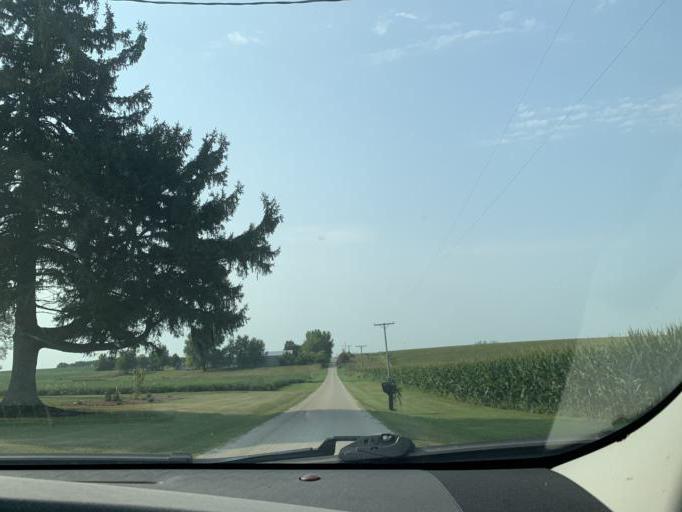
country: US
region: Illinois
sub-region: Whiteside County
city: Morrison
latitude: 41.8555
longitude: -89.8718
